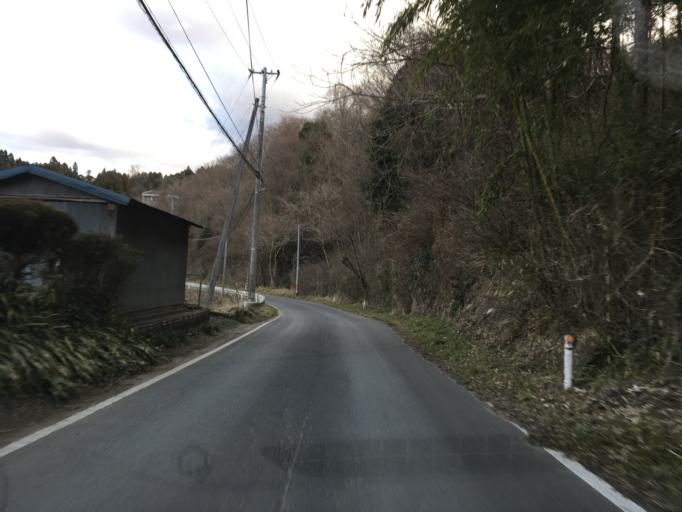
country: JP
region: Miyagi
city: Wakuya
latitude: 38.7136
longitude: 141.2939
